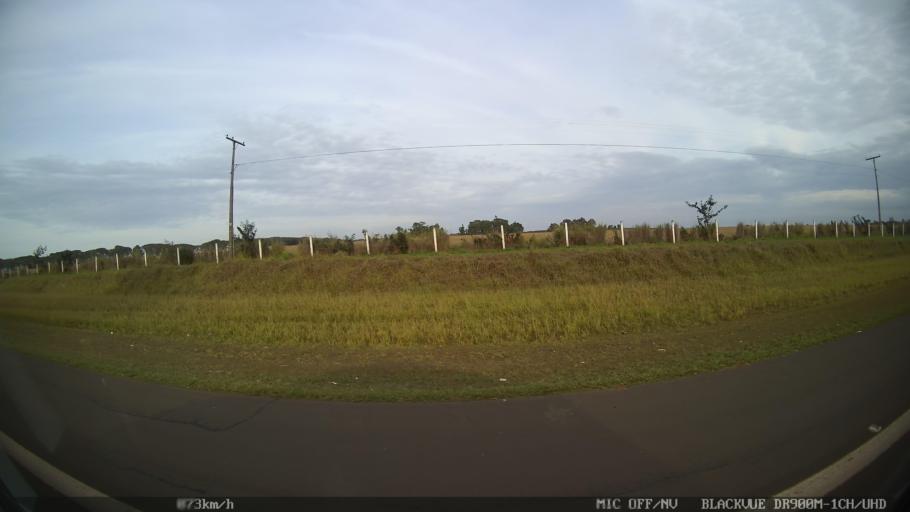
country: BR
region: Sao Paulo
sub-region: Iracemapolis
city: Iracemapolis
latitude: -22.6532
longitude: -47.5177
